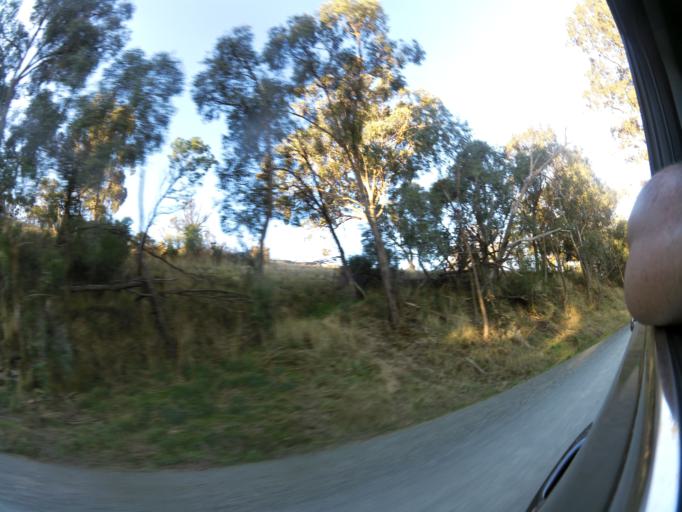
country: AU
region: Victoria
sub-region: Murrindindi
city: Alexandra
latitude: -37.1531
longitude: 145.5297
